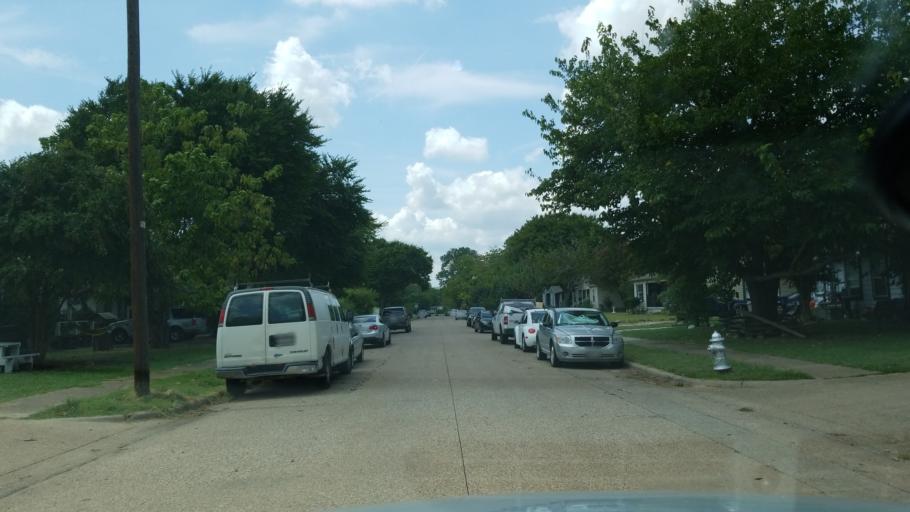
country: US
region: Texas
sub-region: Dallas County
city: Garland
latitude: 32.9189
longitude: -96.6536
